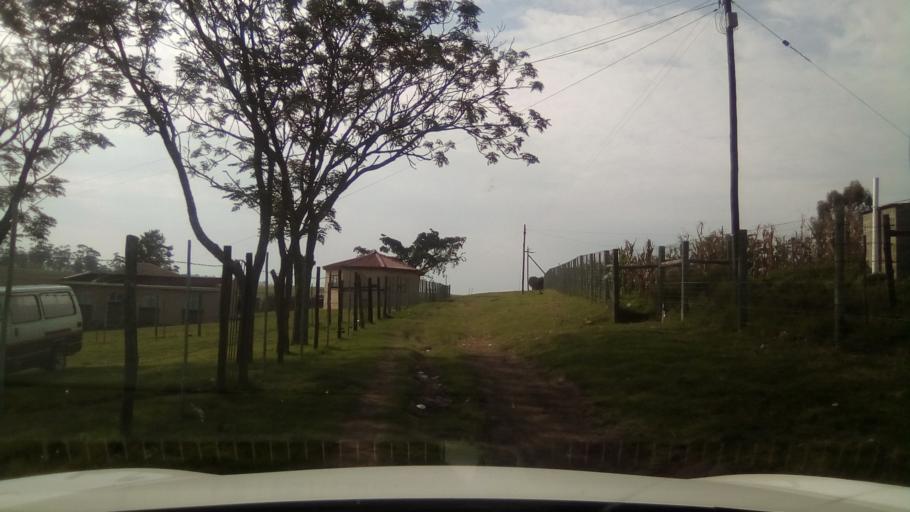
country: ZA
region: Eastern Cape
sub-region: Buffalo City Metropolitan Municipality
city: Bhisho
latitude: -33.0047
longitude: 27.2999
